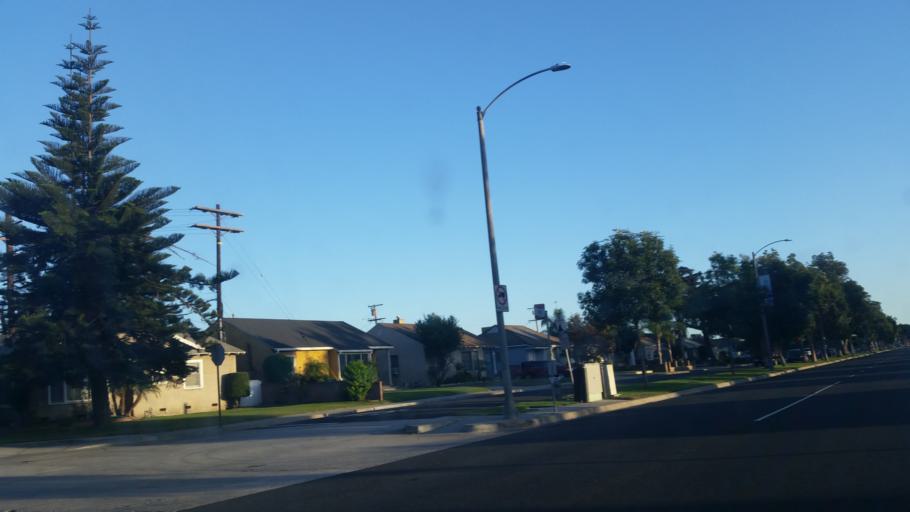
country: US
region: California
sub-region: Los Angeles County
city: Lakewood
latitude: 33.8656
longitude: -118.1252
